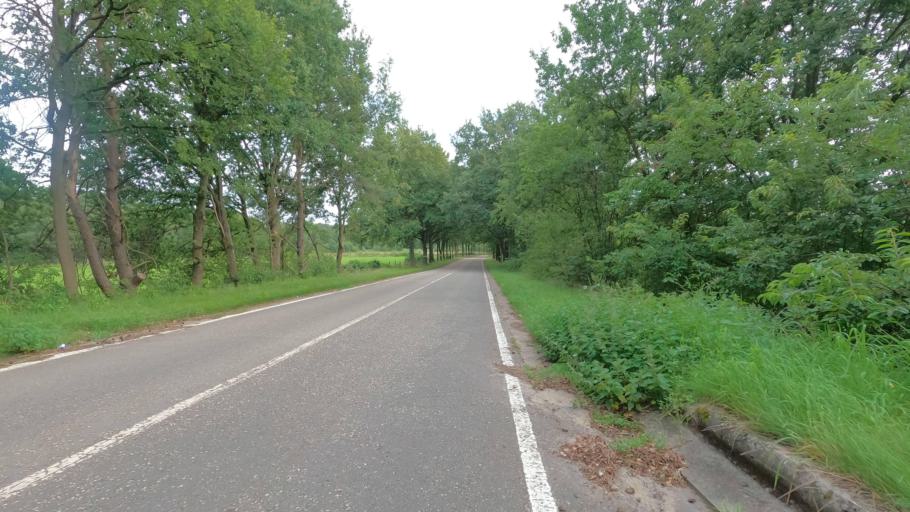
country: BE
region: Flanders
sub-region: Provincie Antwerpen
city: Lille
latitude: 51.2492
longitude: 4.7935
